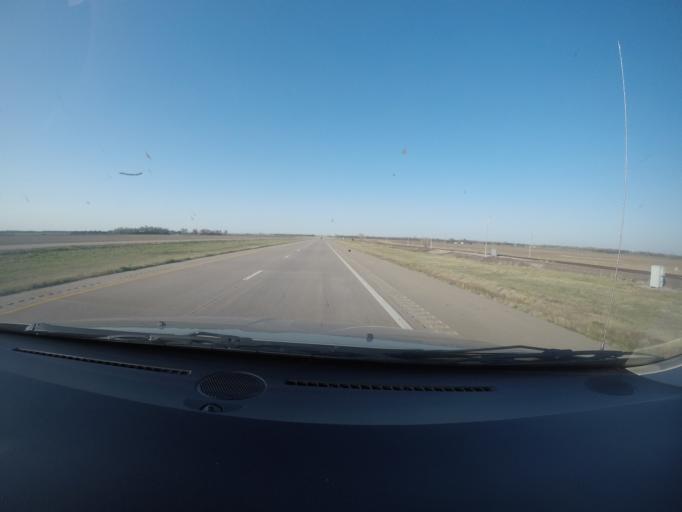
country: US
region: Kansas
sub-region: McPherson County
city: Inman
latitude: 38.2562
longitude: -97.7596
